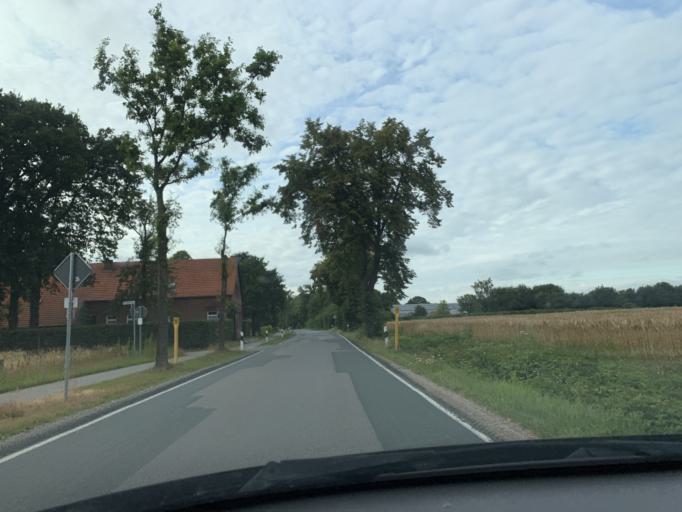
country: DE
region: Lower Saxony
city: Westerstede
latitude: 53.2819
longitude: 7.9256
